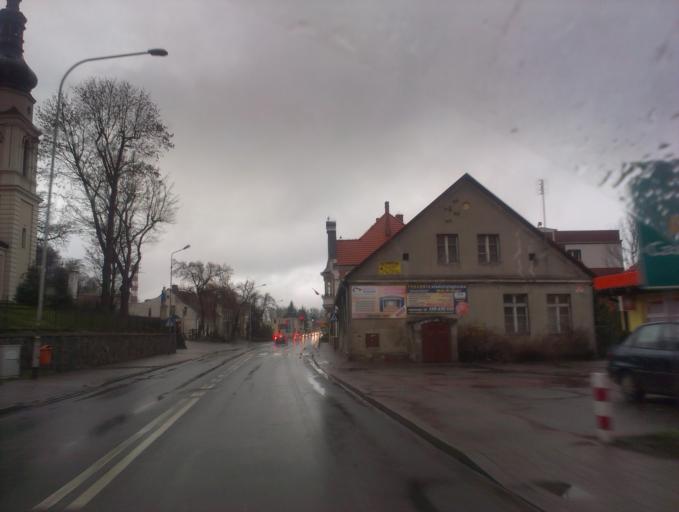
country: PL
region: Greater Poland Voivodeship
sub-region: Powiat pilski
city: Ujscie
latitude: 53.0521
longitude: 16.7346
